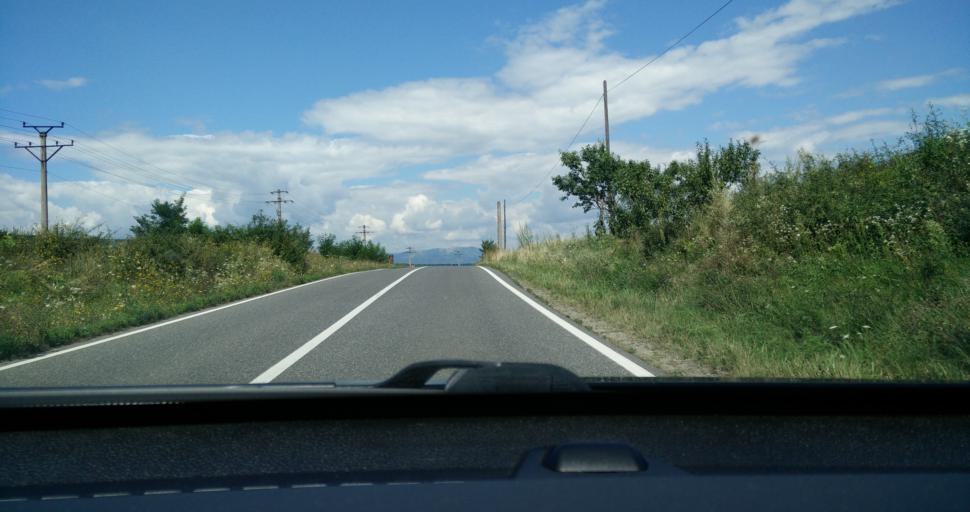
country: RO
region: Alba
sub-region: Comuna Sasciori
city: Sebesel
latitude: 45.8995
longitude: 23.5595
